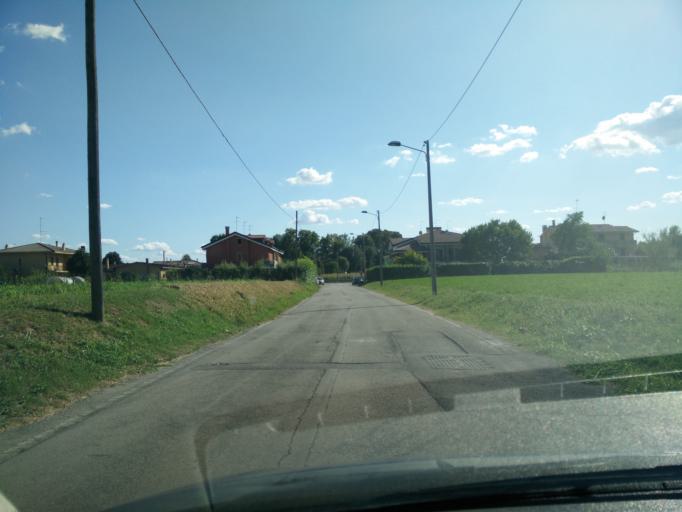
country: IT
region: Veneto
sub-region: Provincia di Padova
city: Mandriola-Sant'Agostino
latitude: 45.3732
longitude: 11.8766
